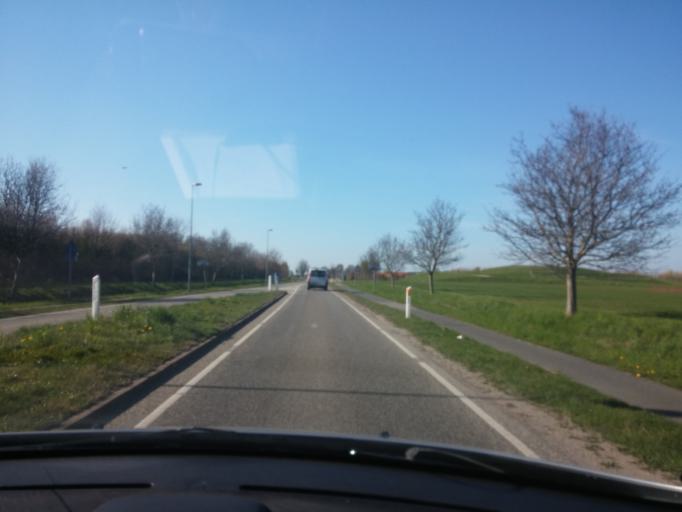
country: DK
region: Central Jutland
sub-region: Odder Kommune
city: Odder
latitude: 55.9201
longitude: 10.2484
